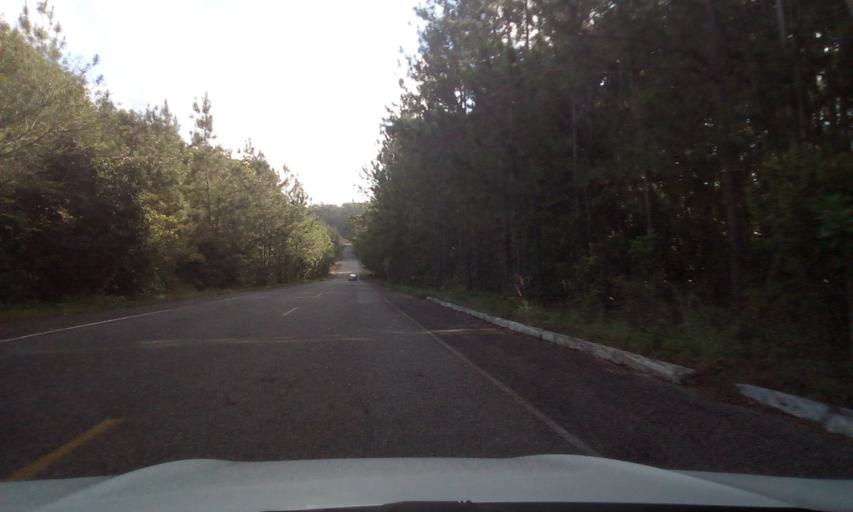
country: BR
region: Bahia
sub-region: Conde
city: Conde
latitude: -12.1014
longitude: -37.7803
